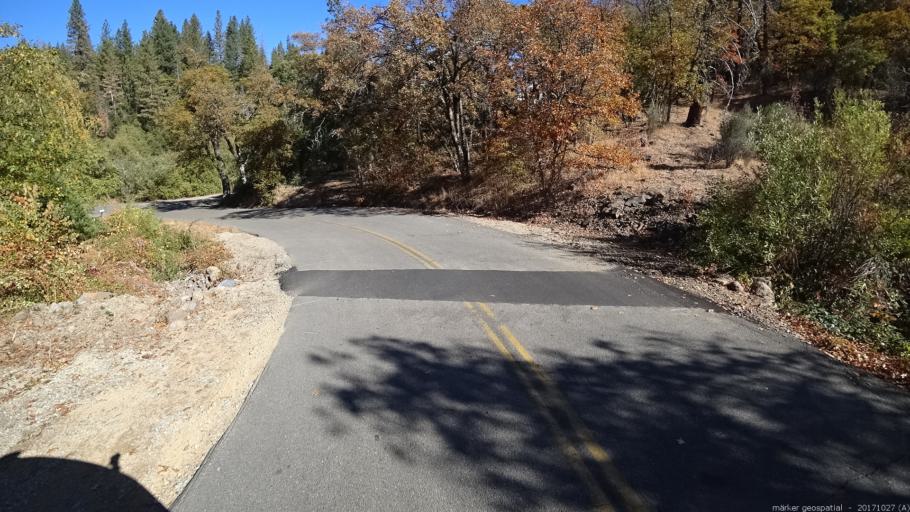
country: US
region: California
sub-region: Shasta County
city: Shingletown
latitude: 40.7483
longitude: -121.9438
